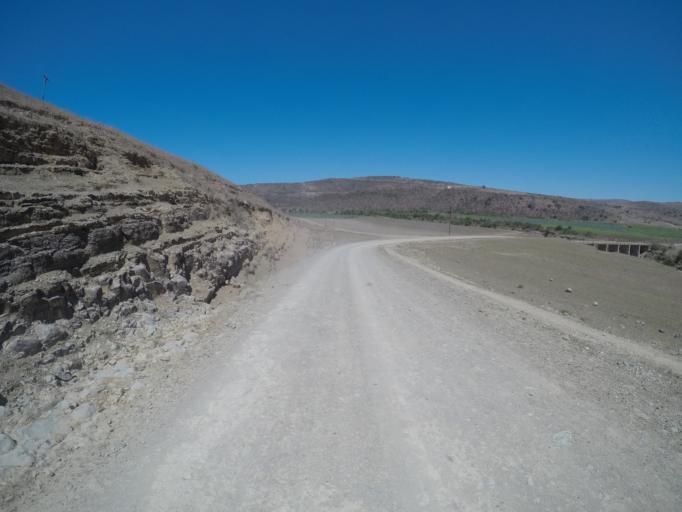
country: ZA
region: Eastern Cape
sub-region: OR Tambo District Municipality
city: Mthatha
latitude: -31.8681
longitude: 28.8723
